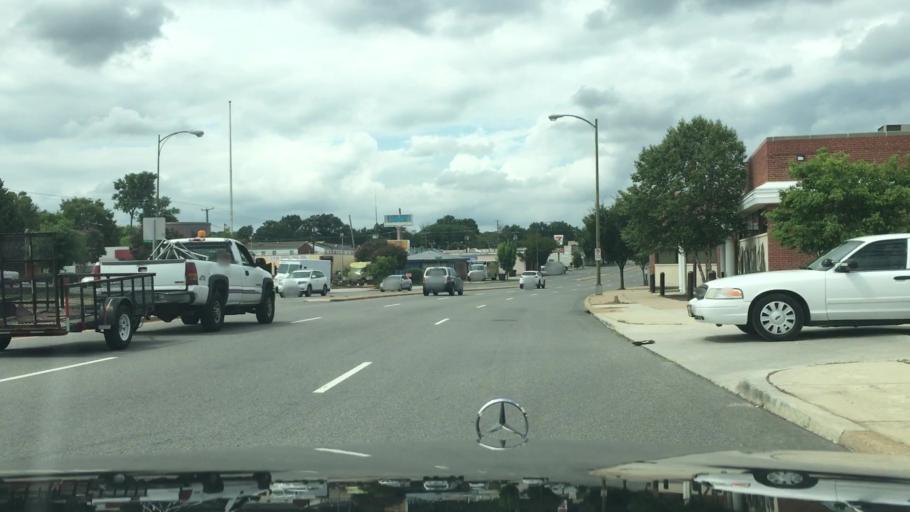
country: US
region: Virginia
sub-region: City of Richmond
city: Richmond
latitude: 37.5630
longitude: -77.4434
